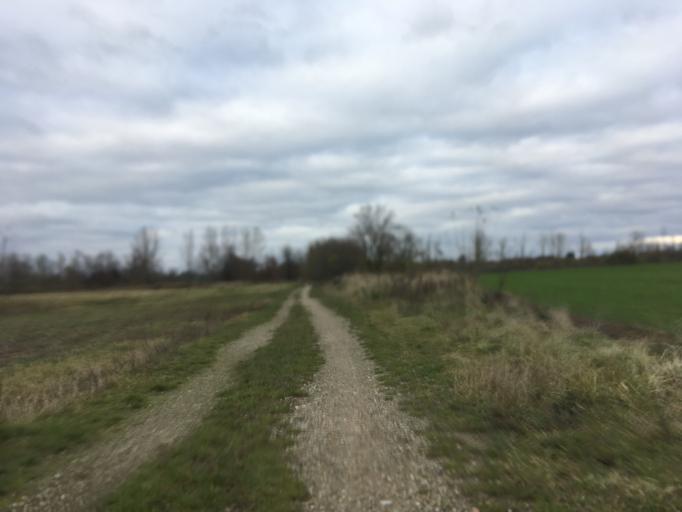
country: DE
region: Berlin
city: Bohnsdorf
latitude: 52.3933
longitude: 13.5527
